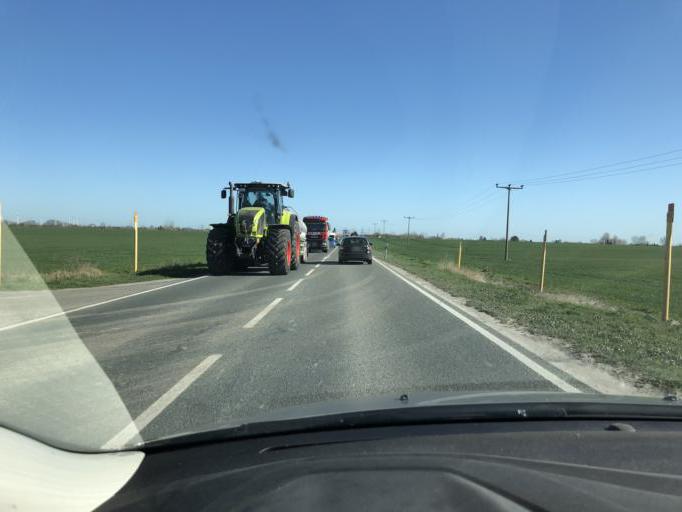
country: DE
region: Saxony-Anhalt
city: Forderstedt
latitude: 51.8851
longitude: 11.6245
